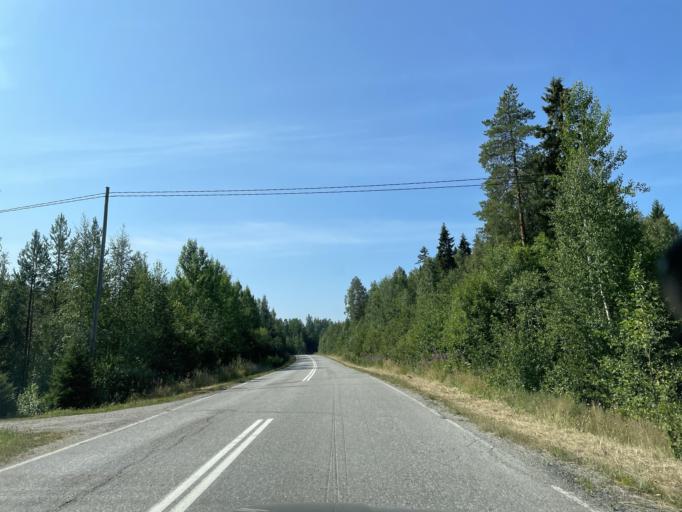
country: FI
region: Central Finland
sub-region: Saarijaervi-Viitasaari
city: Pihtipudas
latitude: 63.3637
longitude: 25.7288
